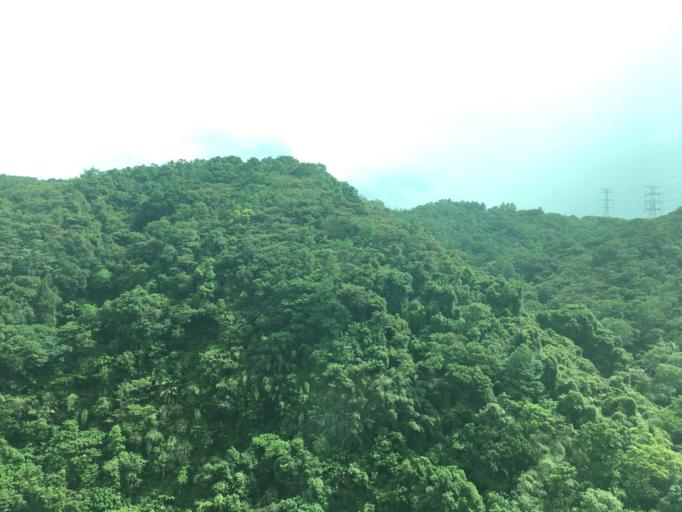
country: TW
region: Taipei
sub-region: Taipei
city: Banqiao
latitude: 25.0313
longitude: 121.3987
